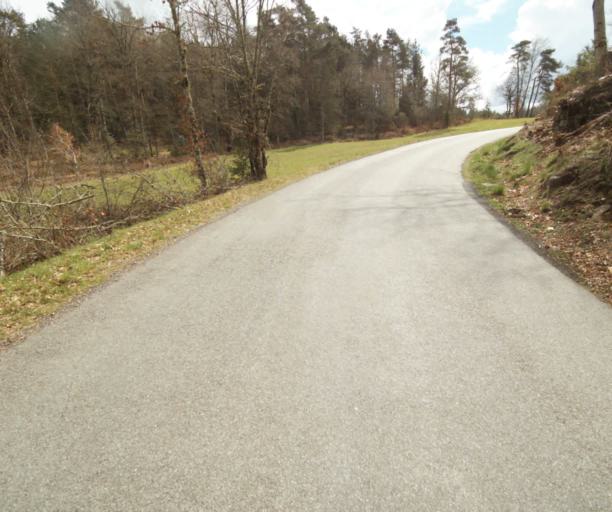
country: FR
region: Limousin
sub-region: Departement de la Correze
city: Correze
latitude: 45.3284
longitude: 1.9169
